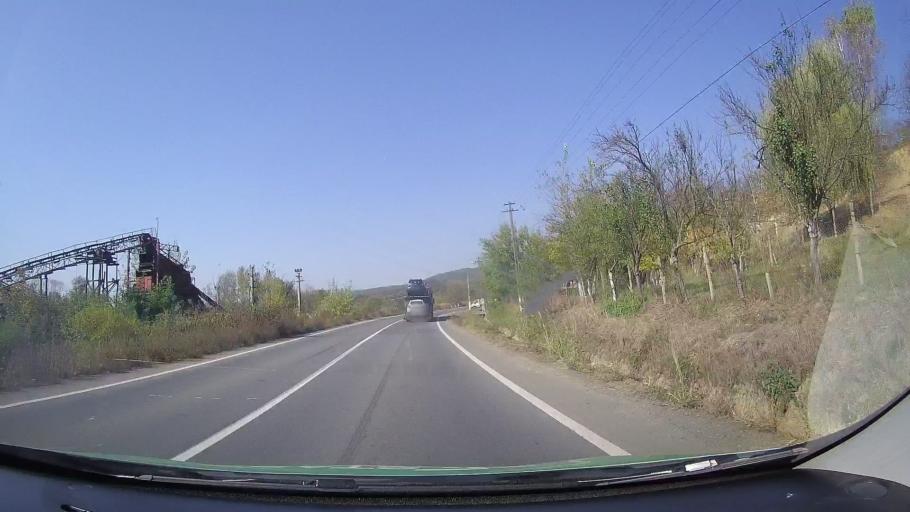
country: RO
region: Arad
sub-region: Comuna Conop
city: Conop
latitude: 46.1051
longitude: 21.8691
